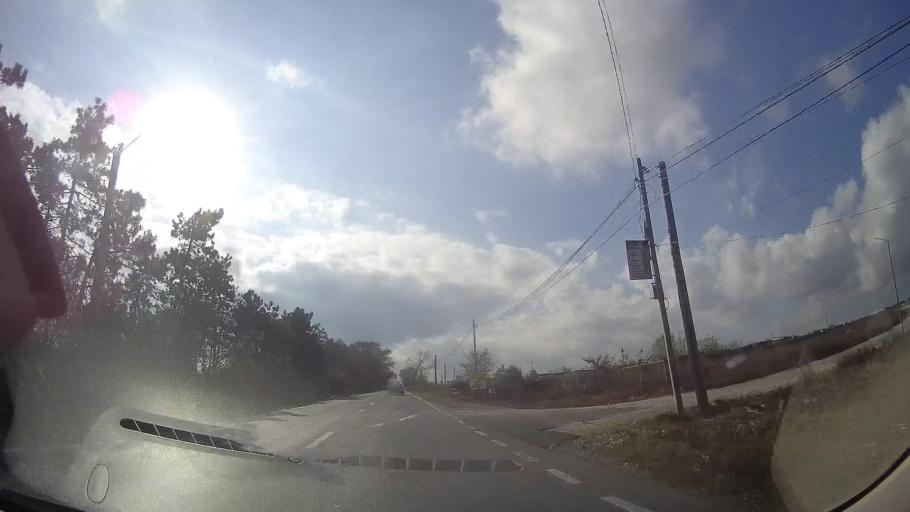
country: RO
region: Constanta
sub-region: Comuna Agigea
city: Agigea
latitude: 44.0858
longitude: 28.6078
